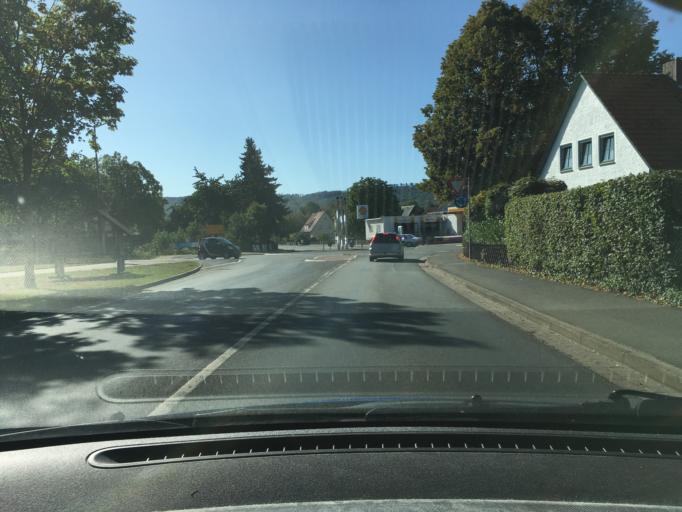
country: DE
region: Lower Saxony
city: Springe
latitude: 52.2110
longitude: 9.5680
